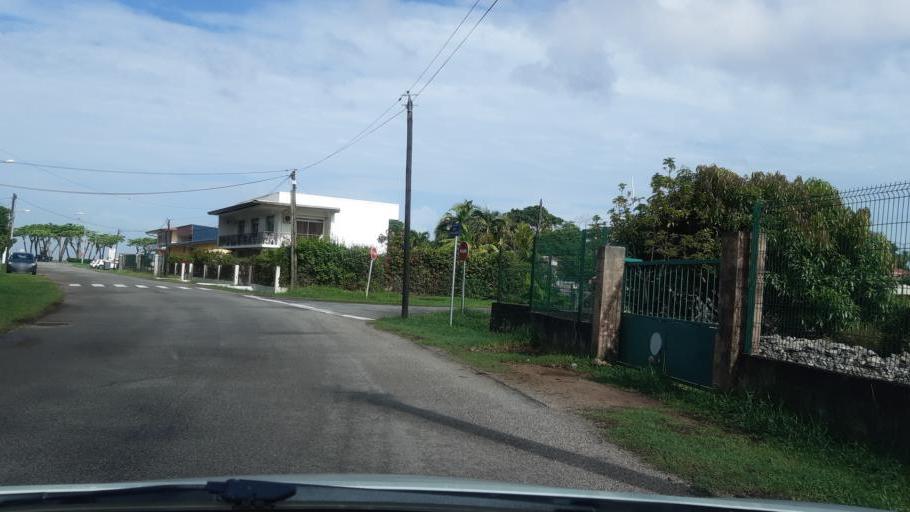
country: GF
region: Guyane
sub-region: Guyane
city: Cayenne
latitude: 4.9425
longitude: -52.3176
